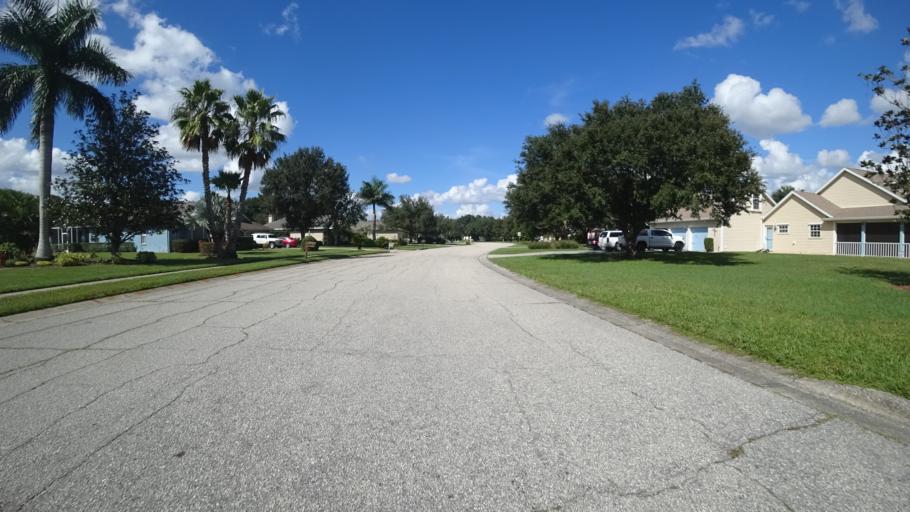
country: US
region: Florida
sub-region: Manatee County
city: Ellenton
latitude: 27.4924
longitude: -82.3948
